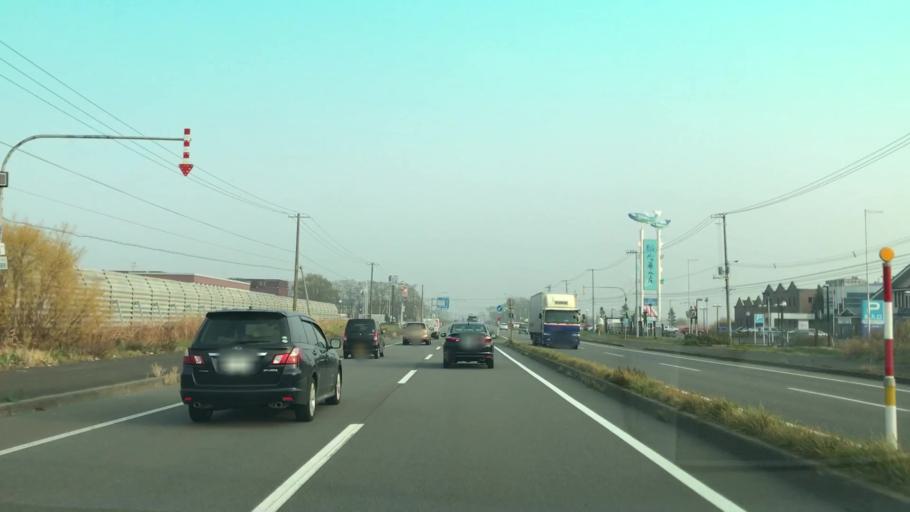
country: JP
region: Hokkaido
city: Ishikari
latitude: 43.2060
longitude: 141.3322
